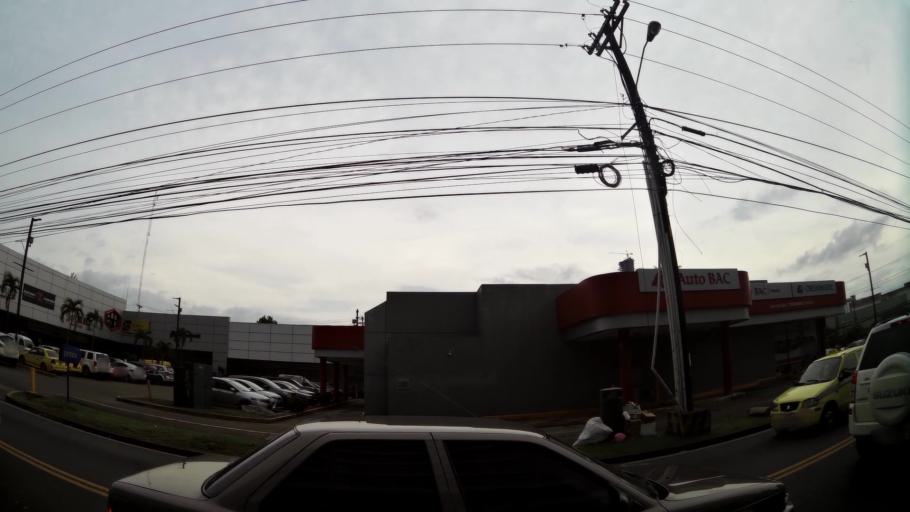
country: PA
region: Panama
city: Panama
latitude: 9.0114
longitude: -79.5340
